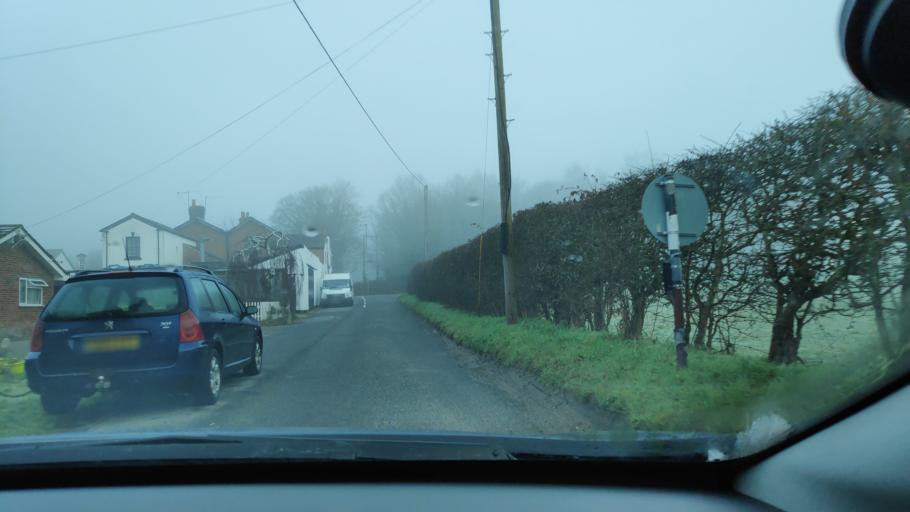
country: GB
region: England
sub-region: Surrey
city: Seale
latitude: 51.2516
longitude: -0.7062
